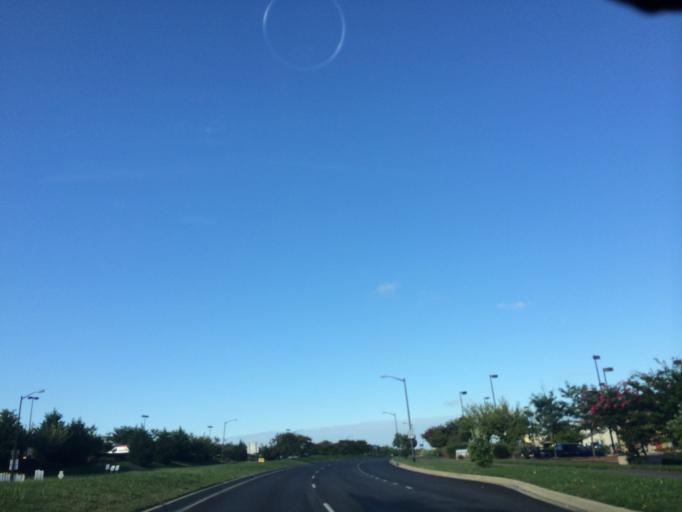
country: US
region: Maryland
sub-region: Anne Arundel County
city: Severn
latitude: 39.1537
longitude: -76.7217
